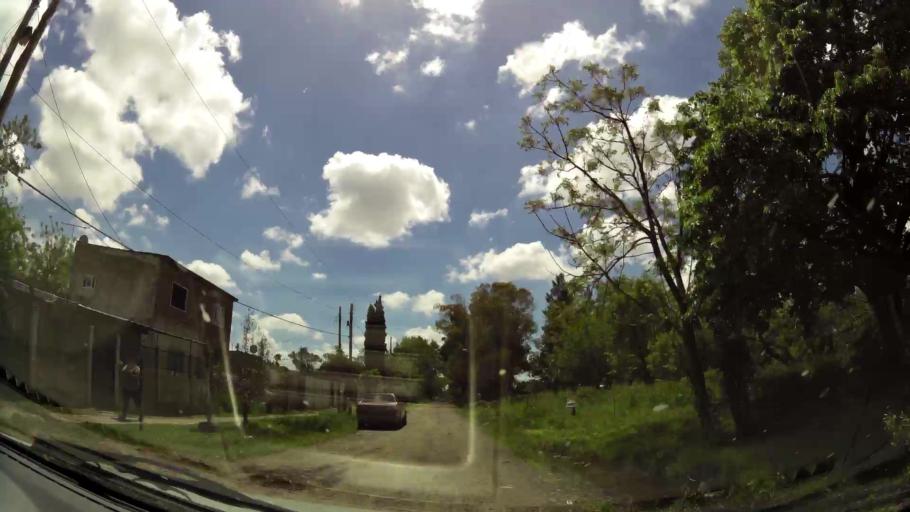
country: AR
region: Buenos Aires
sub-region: Partido de Quilmes
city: Quilmes
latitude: -34.8182
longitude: -58.2398
